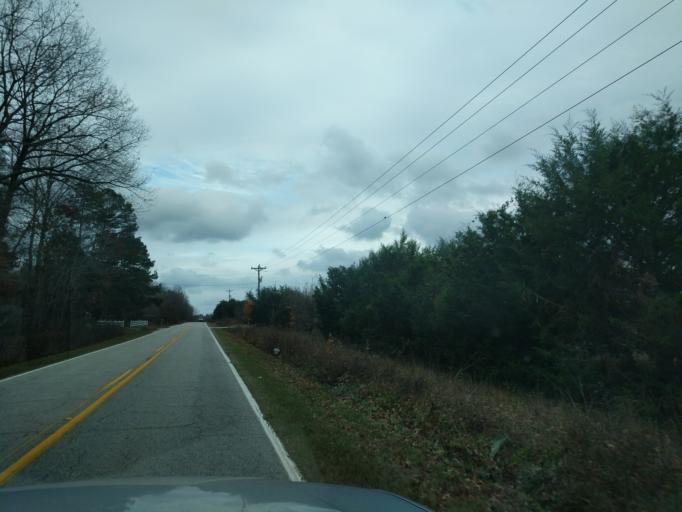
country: US
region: South Carolina
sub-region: Laurens County
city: Laurens
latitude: 34.4144
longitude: -82.0970
